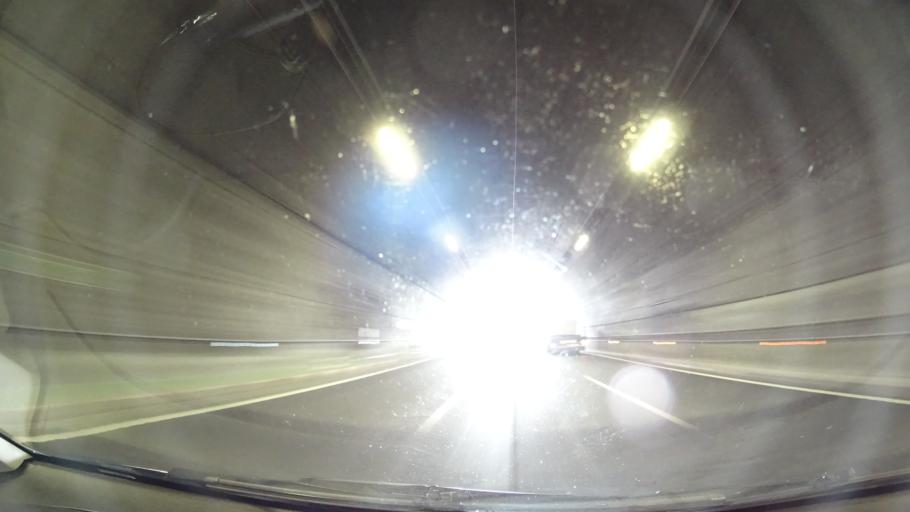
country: ES
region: Madrid
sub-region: Provincia de Madrid
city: Somosierra
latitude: 41.1366
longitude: -3.5823
